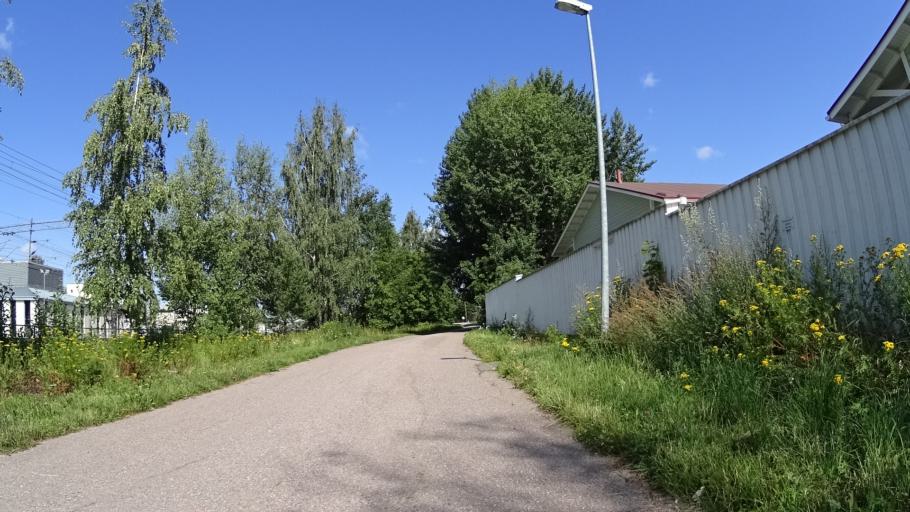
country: FI
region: Uusimaa
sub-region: Helsinki
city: Jaervenpaeae
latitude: 60.4704
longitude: 25.0961
